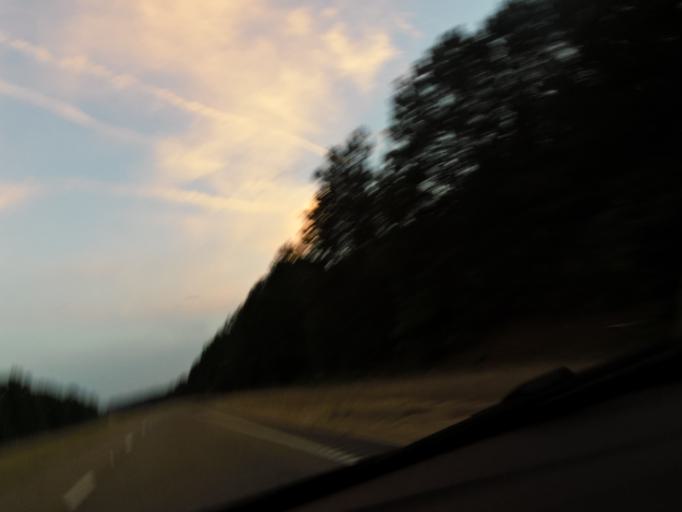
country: US
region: Mississippi
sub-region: Lauderdale County
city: Meridian Station
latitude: 32.5971
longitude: -88.5001
